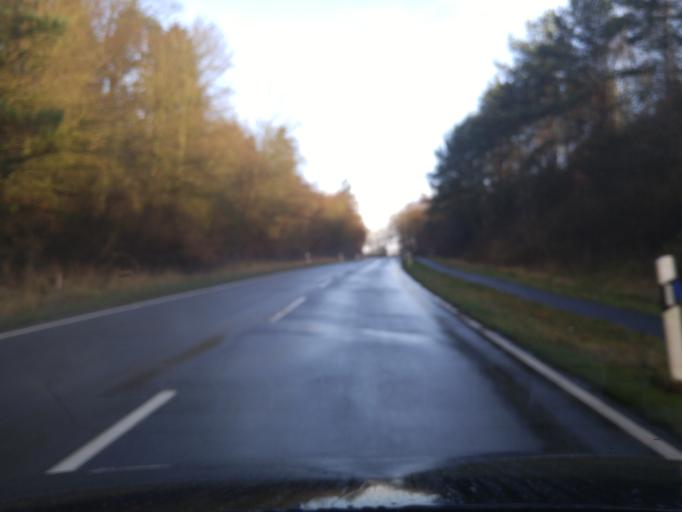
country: DE
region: Schleswig-Holstein
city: Ratekau
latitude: 53.9357
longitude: 10.7339
